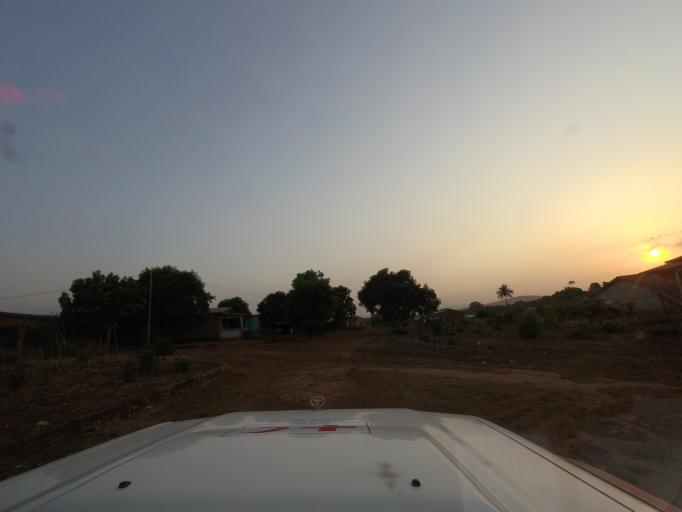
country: GN
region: Kindia
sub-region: Kindia
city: Kindia
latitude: 10.0158
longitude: -12.8913
